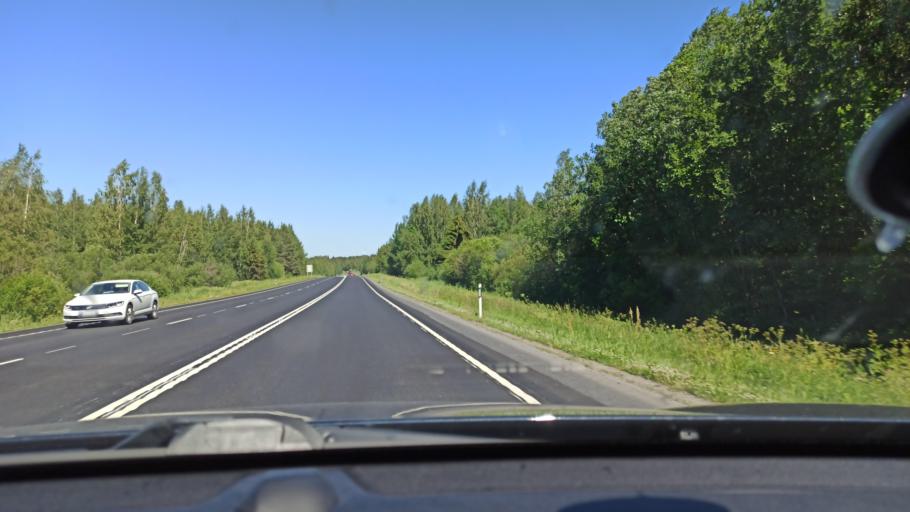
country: FI
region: Ostrobothnia
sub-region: Vaasa
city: Oravais
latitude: 63.2769
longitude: 22.3366
